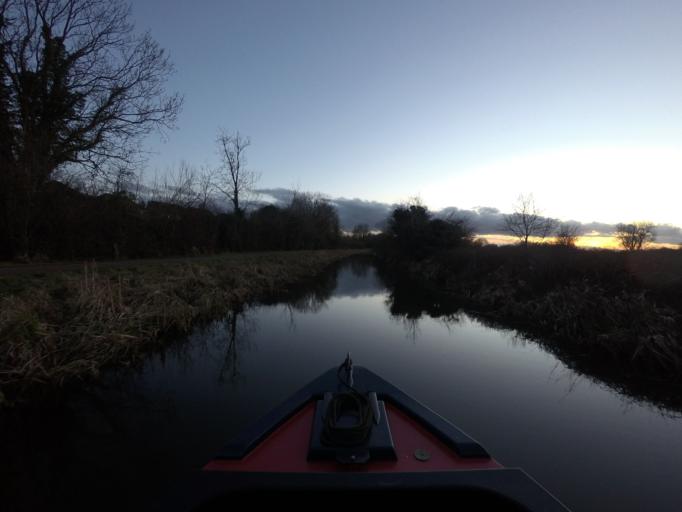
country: GB
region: England
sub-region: Northamptonshire
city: Hardingstone
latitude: 52.2276
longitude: -0.9316
